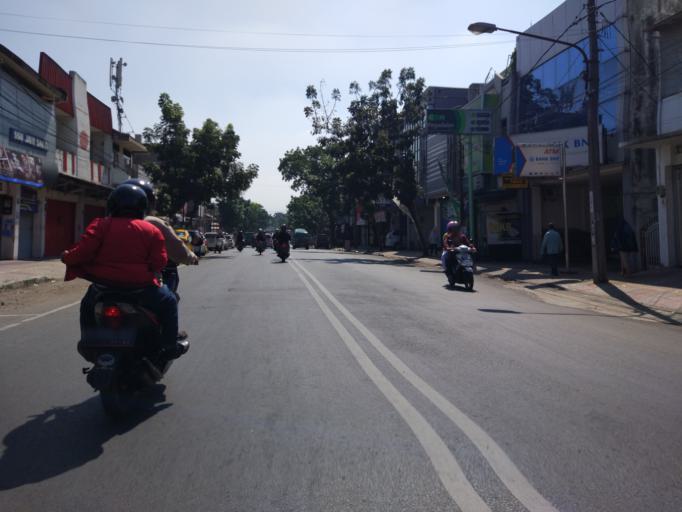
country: ID
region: West Java
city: Bandung
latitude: -6.9321
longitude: 107.5968
